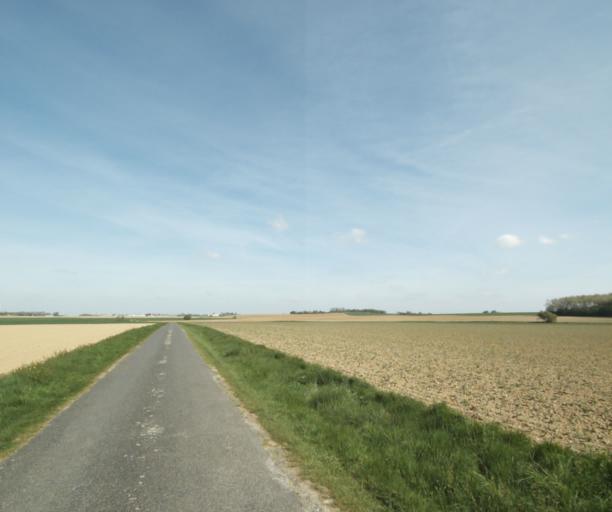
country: FR
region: Ile-de-France
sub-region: Departement de Seine-et-Marne
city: Nangis
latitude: 48.5414
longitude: 3.0370
